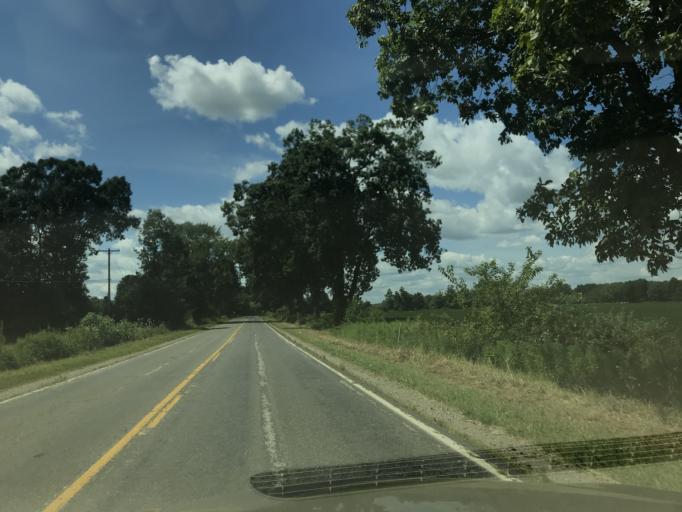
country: US
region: Michigan
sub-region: Ingham County
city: Leslie
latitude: 42.4512
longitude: -84.4768
